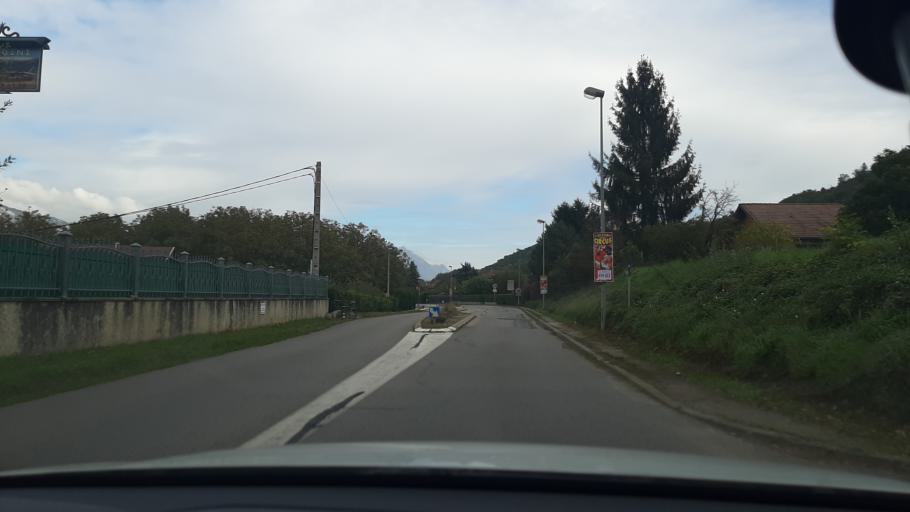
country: FR
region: Rhone-Alpes
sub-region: Departement de l'Isere
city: Pontcharra
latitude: 45.4445
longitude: 6.0348
